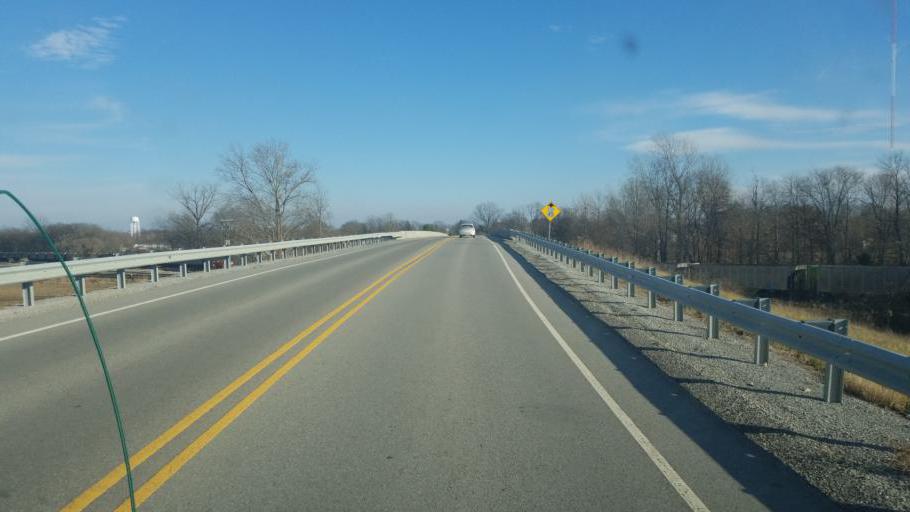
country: US
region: Illinois
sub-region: Wabash County
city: Mount Carmel
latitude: 38.4009
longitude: -87.7918
